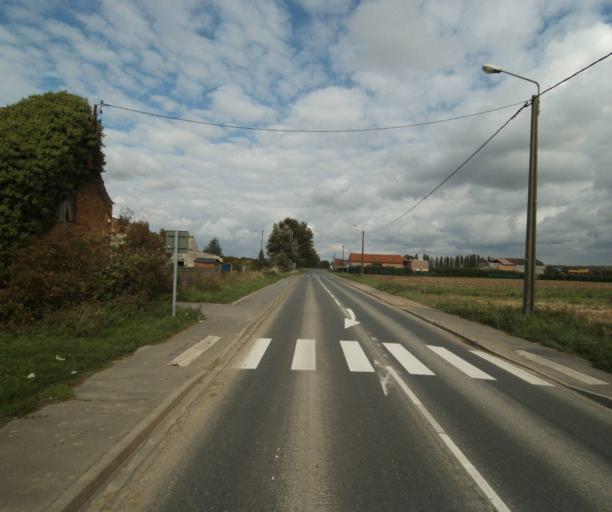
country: FR
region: Nord-Pas-de-Calais
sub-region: Departement du Nord
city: Premesques
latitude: 50.6656
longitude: 2.9392
